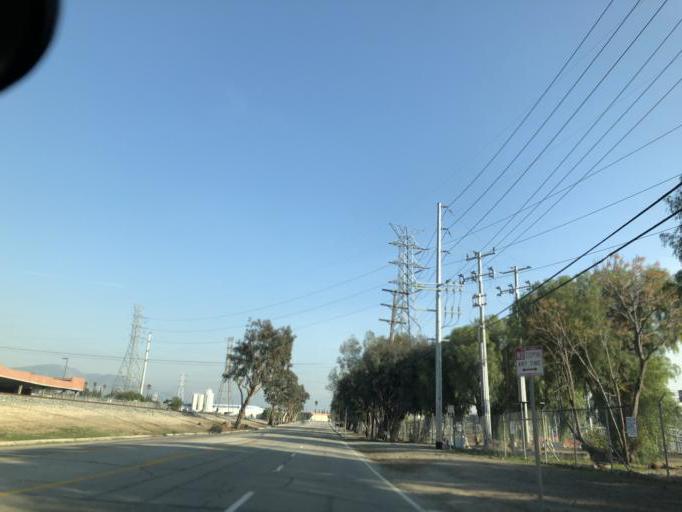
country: US
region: California
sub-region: Los Angeles County
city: San Fernando
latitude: 34.3138
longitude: -118.4833
